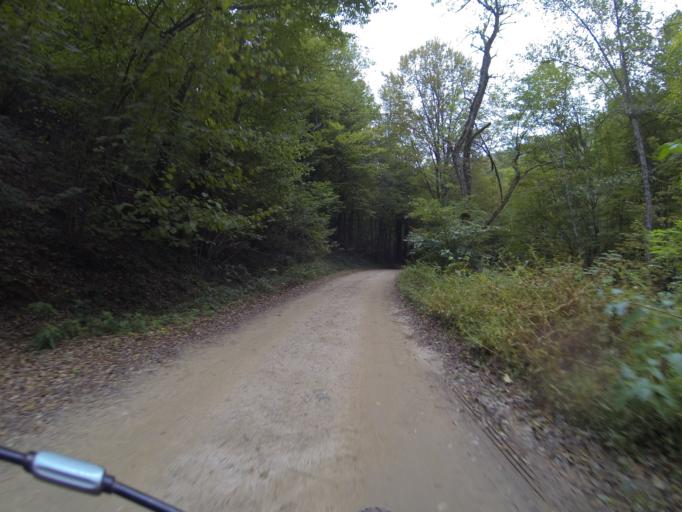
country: RO
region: Gorj
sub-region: Comuna Tismana
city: Pocruia
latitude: 45.0557
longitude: 22.9067
